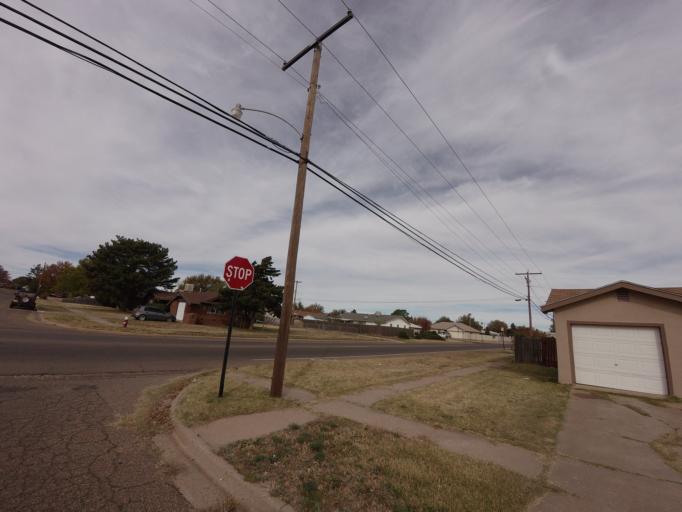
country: US
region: New Mexico
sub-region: Curry County
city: Clovis
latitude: 34.4247
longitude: -103.2140
